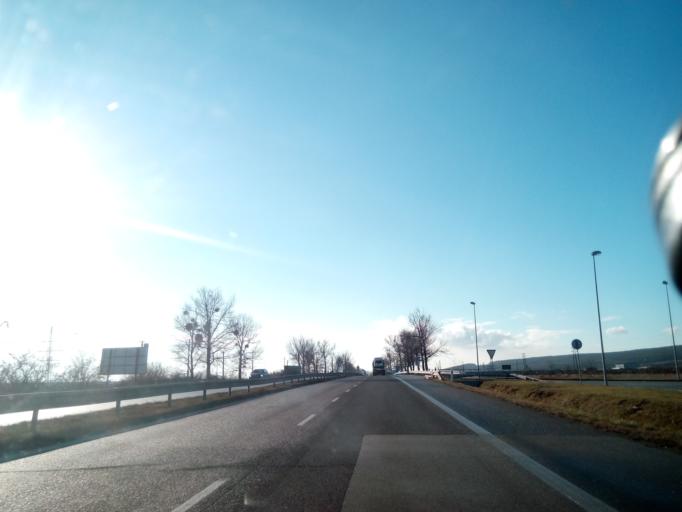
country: SK
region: Kosicky
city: Kosice
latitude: 48.6652
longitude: 21.2087
